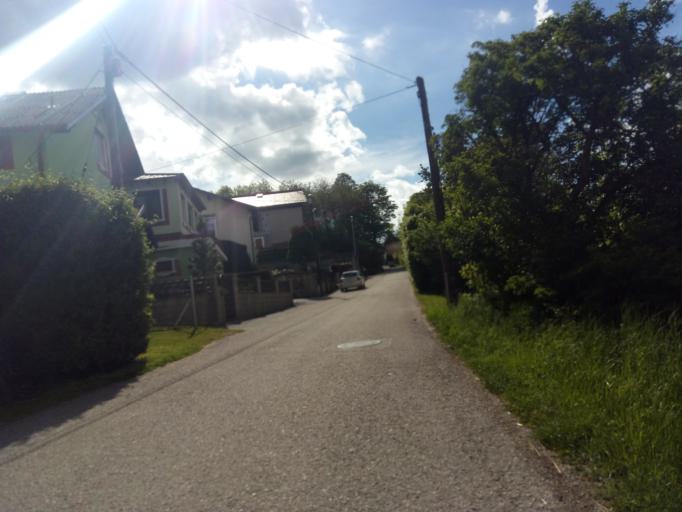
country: AT
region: Lower Austria
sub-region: Politischer Bezirk Modling
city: Breitenfurt bei Wien
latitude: 48.1335
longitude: 16.1478
